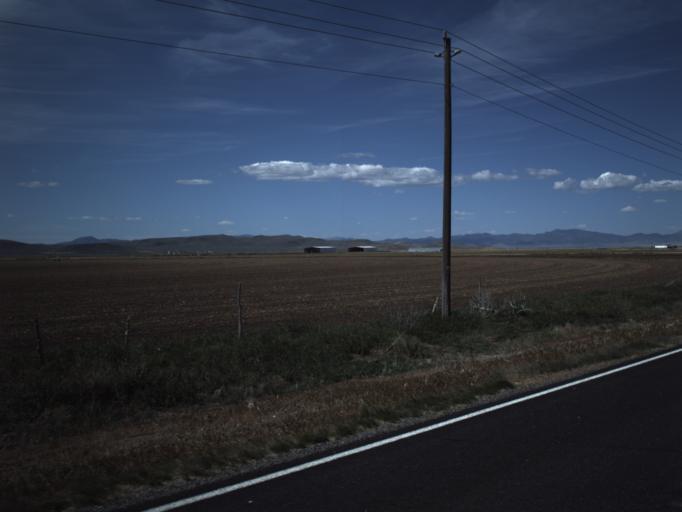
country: US
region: Utah
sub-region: Washington County
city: Enterprise
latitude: 37.6373
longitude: -113.6612
